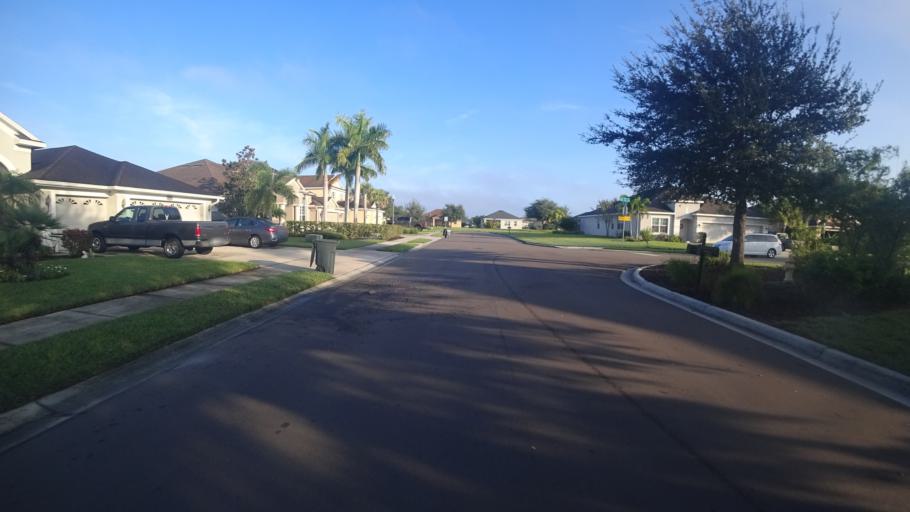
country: US
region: Florida
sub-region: Manatee County
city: Ellenton
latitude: 27.5319
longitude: -82.4137
